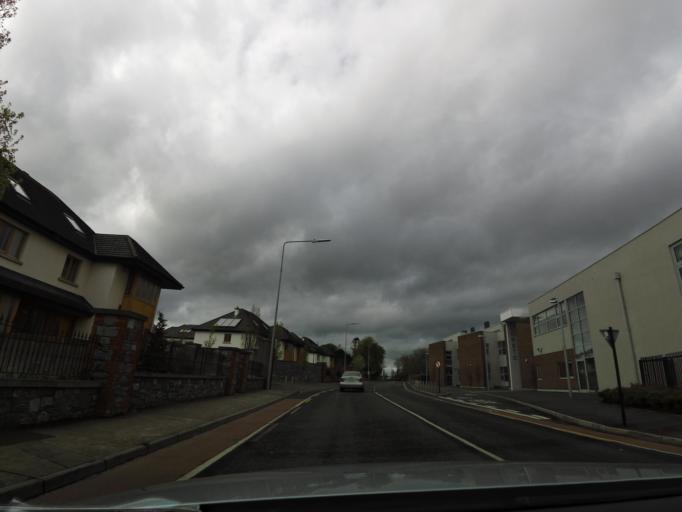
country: IE
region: Leinster
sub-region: Kilkenny
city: Kilkenny
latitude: 52.6584
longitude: -7.2613
